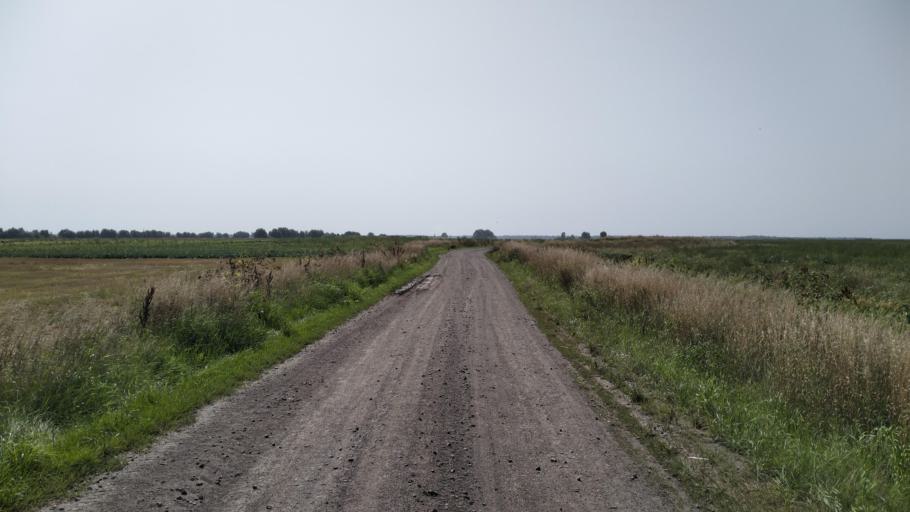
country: BY
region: Brest
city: Davyd-Haradok
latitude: 52.0075
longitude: 27.1670
